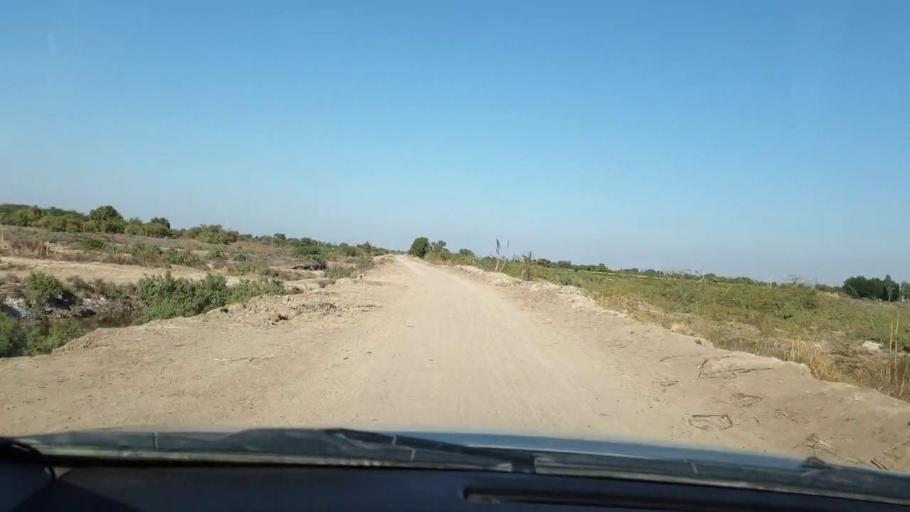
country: PK
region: Sindh
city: Berani
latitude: 25.7202
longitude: 68.9886
